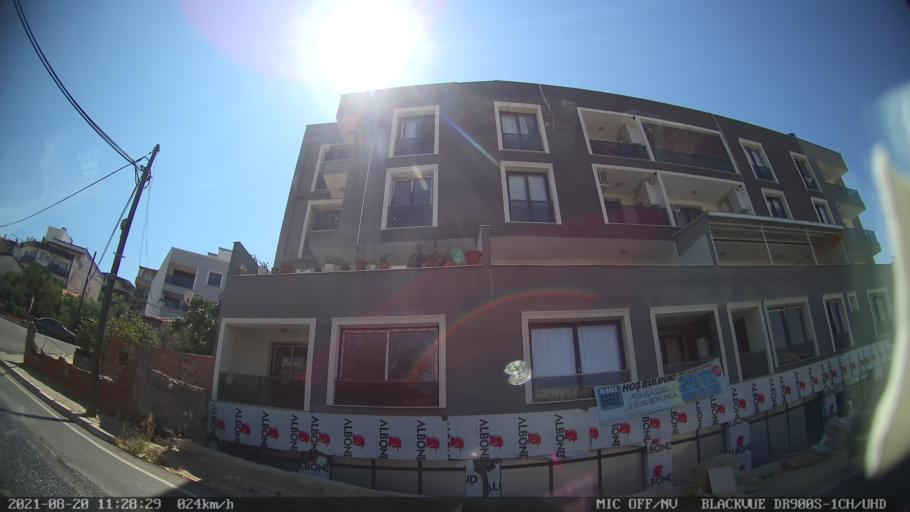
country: TR
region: Izmir
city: Karsiyaka
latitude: 38.5003
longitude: 27.0709
